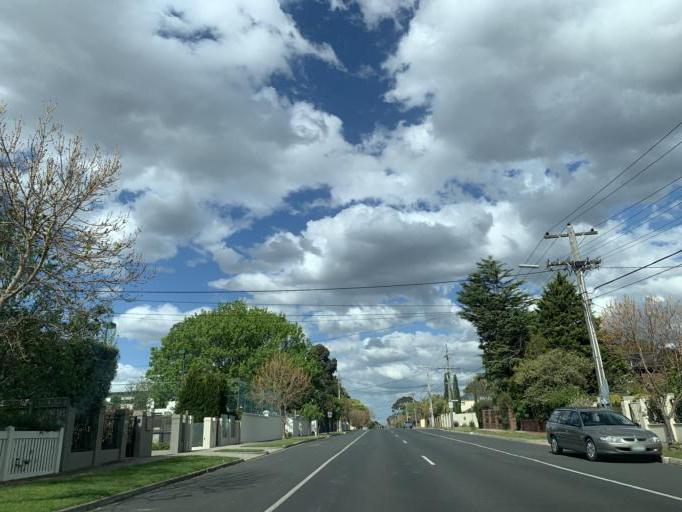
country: AU
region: Victoria
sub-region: Bayside
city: North Brighton
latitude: -37.9187
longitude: 145.0088
